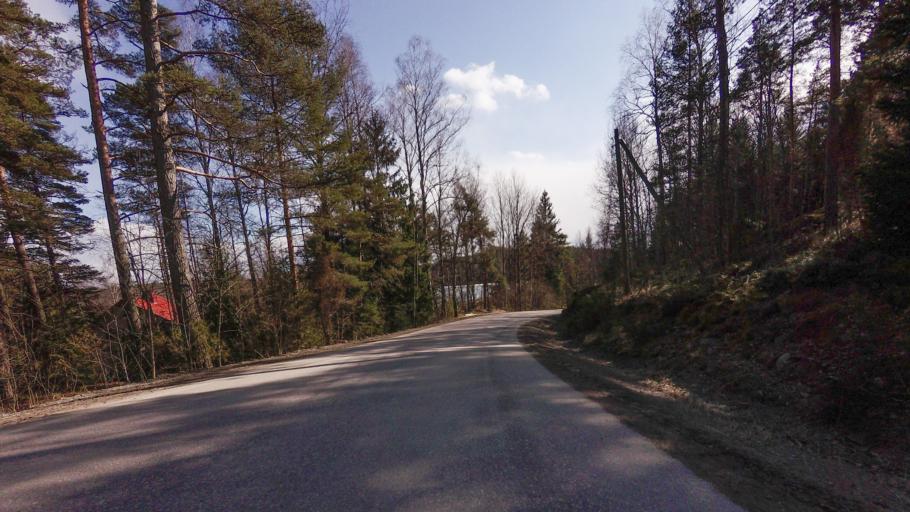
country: FI
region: Varsinais-Suomi
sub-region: Salo
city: Suomusjaervi
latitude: 60.3207
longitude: 23.6520
